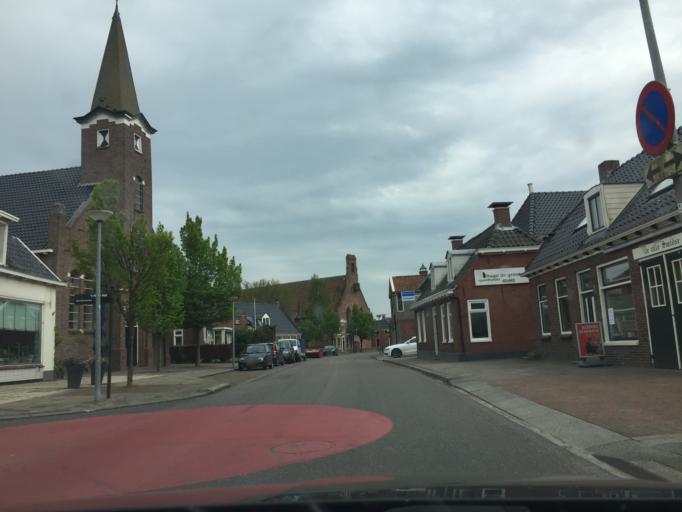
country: NL
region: Groningen
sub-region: Gemeente Zuidhorn
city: Aduard
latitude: 53.2574
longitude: 6.4587
